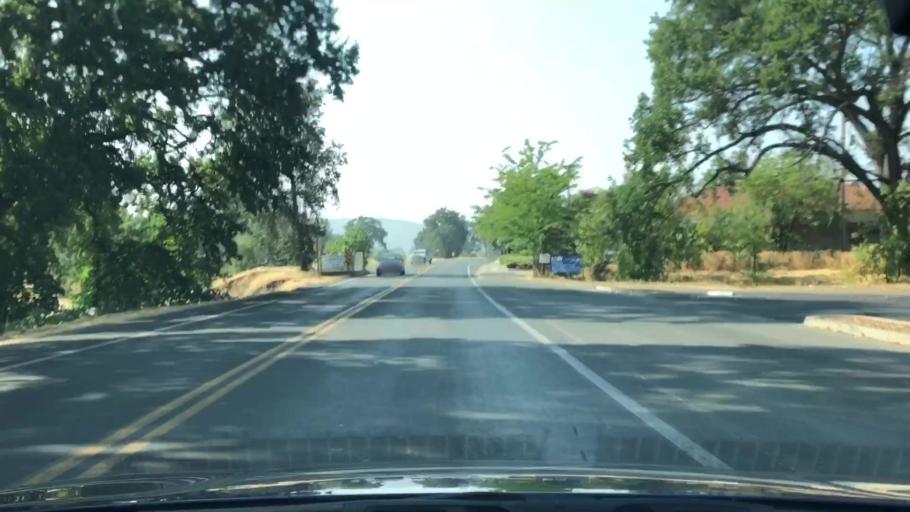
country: US
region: California
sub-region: Lake County
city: Hidden Valley Lake
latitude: 38.7955
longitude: -122.5554
